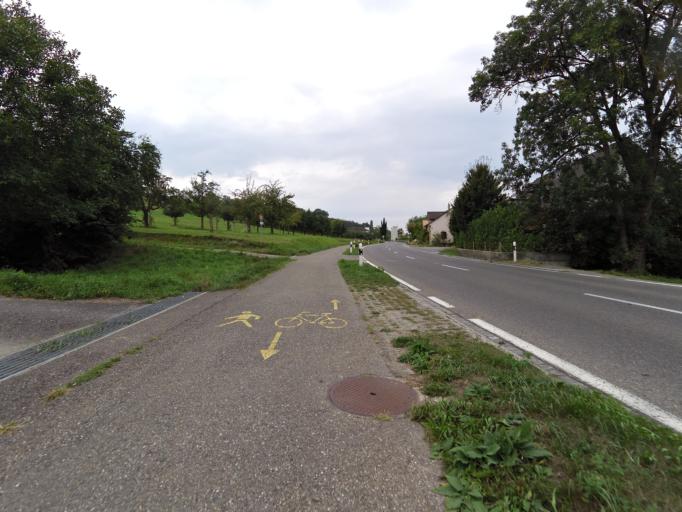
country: CH
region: Thurgau
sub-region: Kreuzlingen District
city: Ermatingen
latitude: 47.6640
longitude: 9.0998
